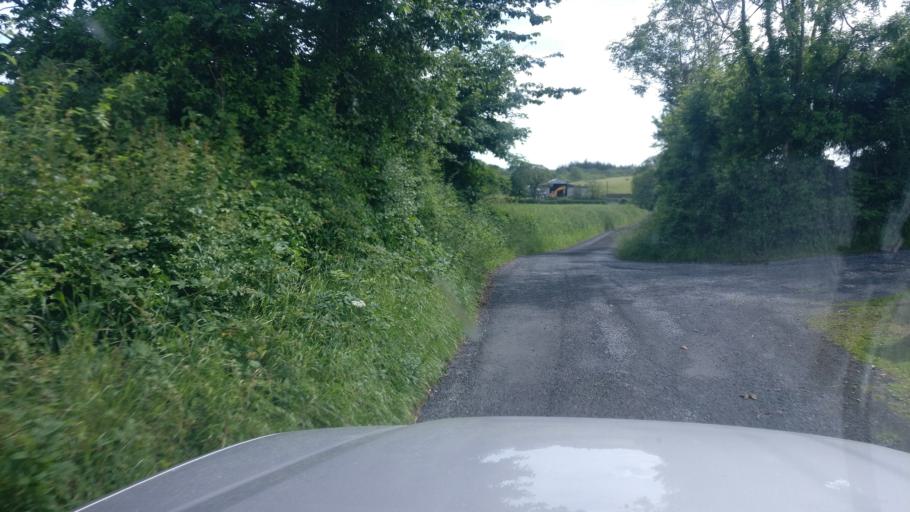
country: IE
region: Connaught
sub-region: County Galway
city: Gort
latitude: 53.0775
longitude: -8.7726
